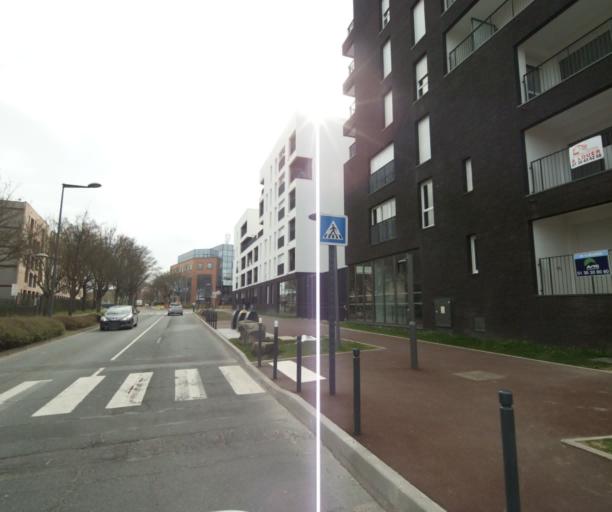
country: FR
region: Ile-de-France
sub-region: Departement du Val-d'Oise
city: Vaureal
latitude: 49.0509
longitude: 2.0376
